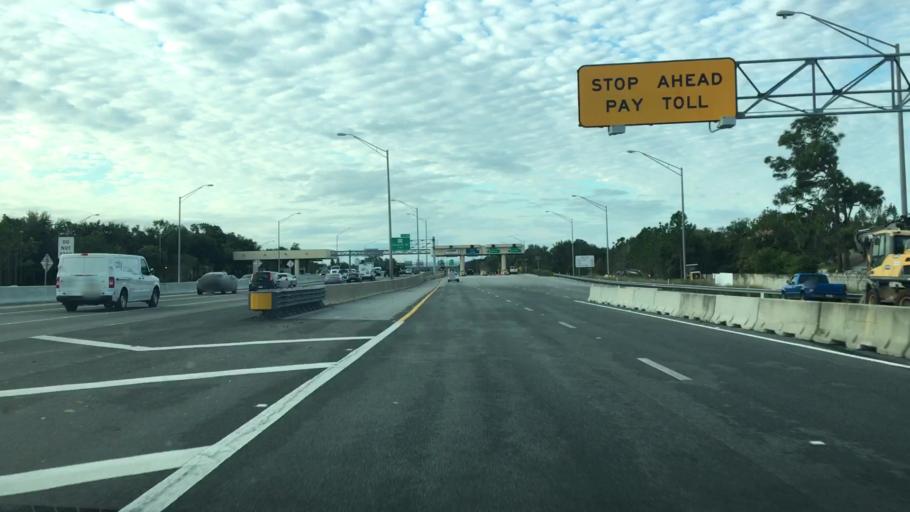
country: US
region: Florida
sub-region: Orange County
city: Union Park
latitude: 28.5894
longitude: -81.2543
